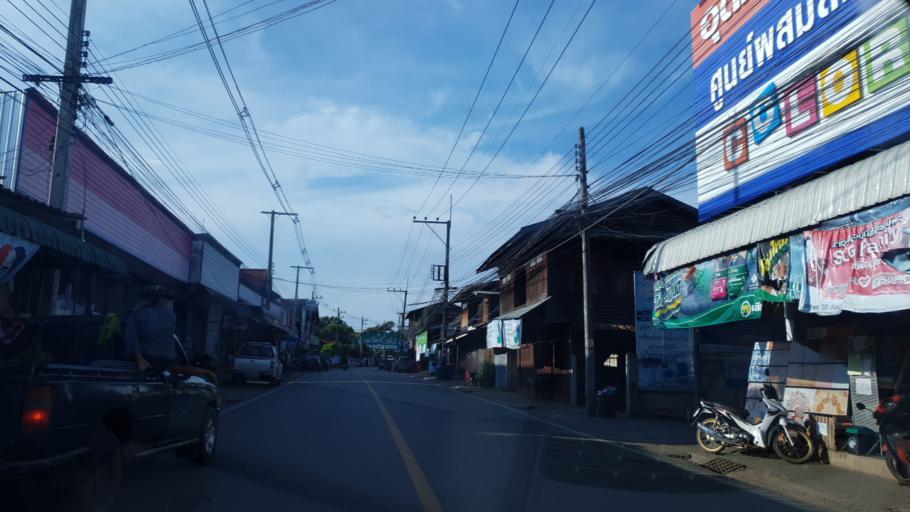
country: TH
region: Mae Hong Son
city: Khun Yuam
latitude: 18.8265
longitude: 97.9333
